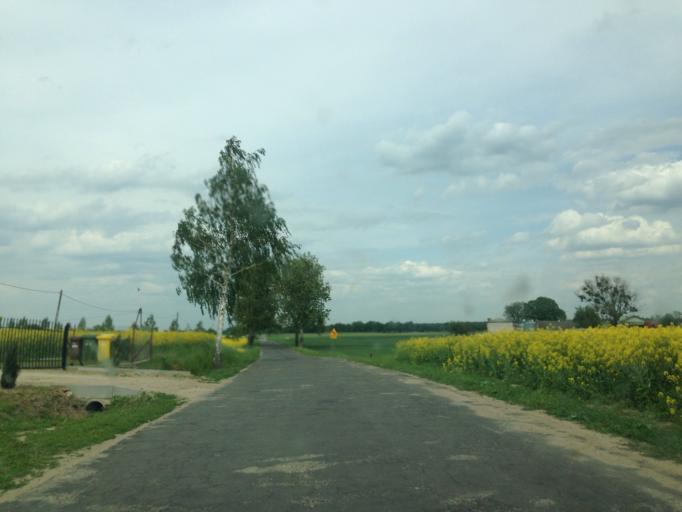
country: PL
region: Kujawsko-Pomorskie
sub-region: Powiat brodnicki
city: Bobrowo
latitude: 53.2852
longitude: 19.3305
